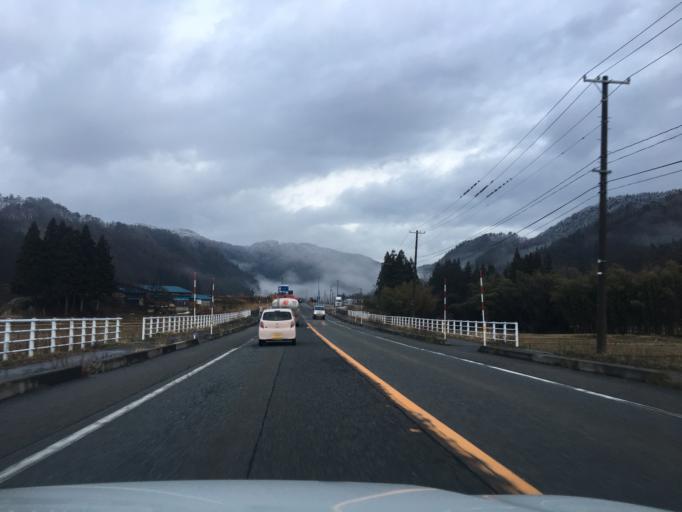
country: JP
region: Niigata
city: Murakami
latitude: 38.4416
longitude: 139.5888
